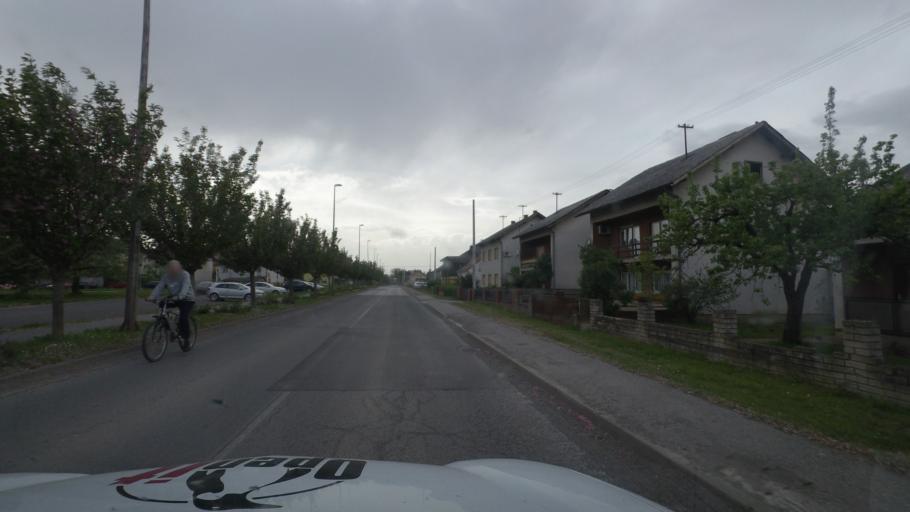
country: HR
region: Sisacko-Moslavacka
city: Glina
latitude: 45.3336
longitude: 16.0935
